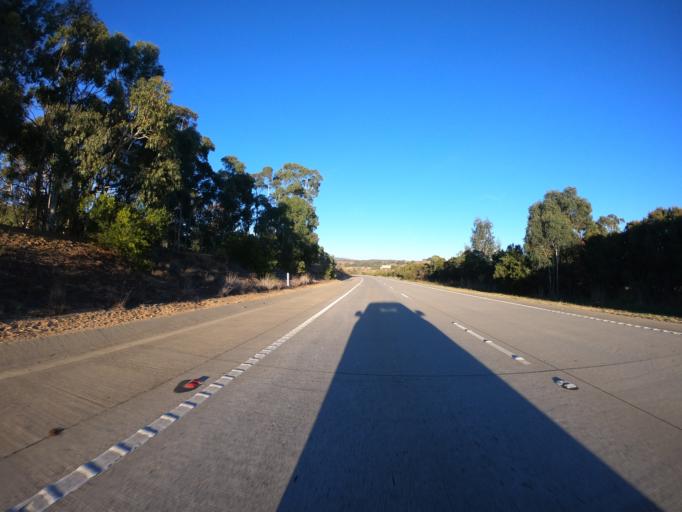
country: AU
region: New South Wales
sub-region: Yass Valley
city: Gundaroo
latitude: -35.1163
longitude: 149.3534
